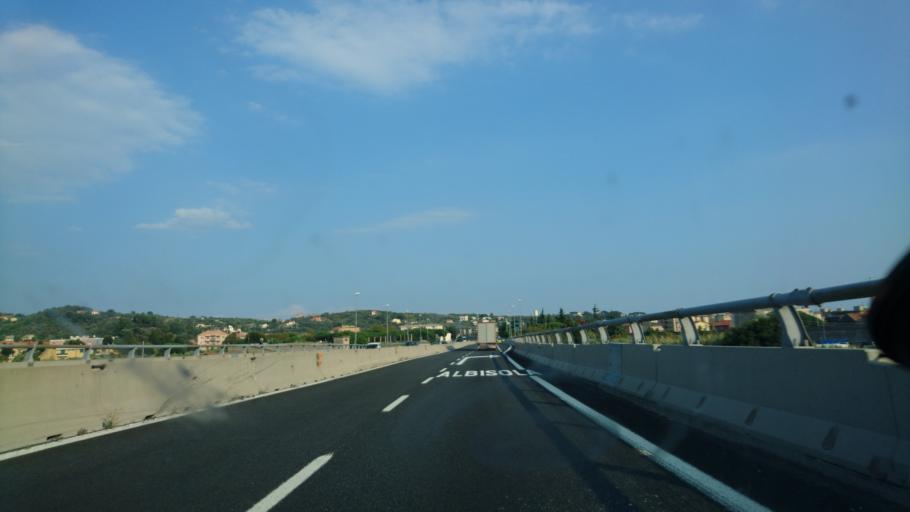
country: IT
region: Liguria
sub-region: Provincia di Savona
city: Albisola Marina
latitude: 44.3350
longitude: 8.5049
